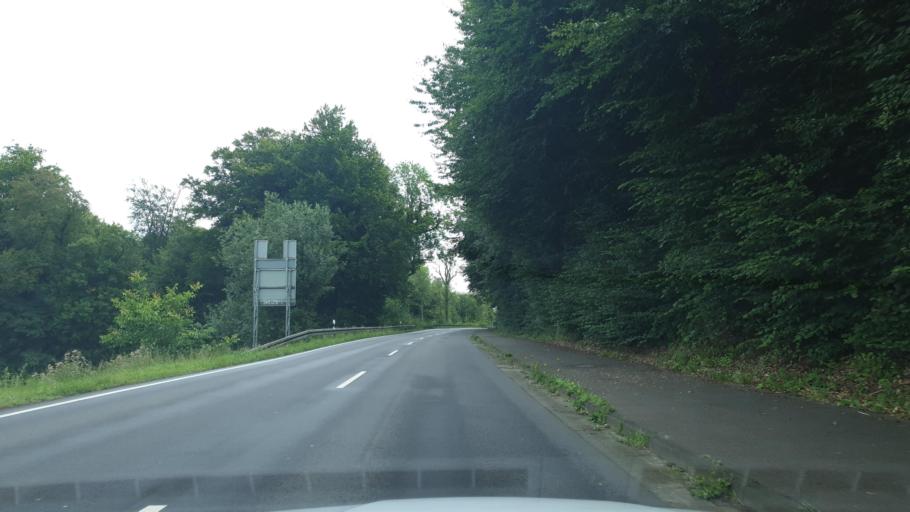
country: DE
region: Lower Saxony
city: Bissendorf
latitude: 52.2021
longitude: 8.1319
